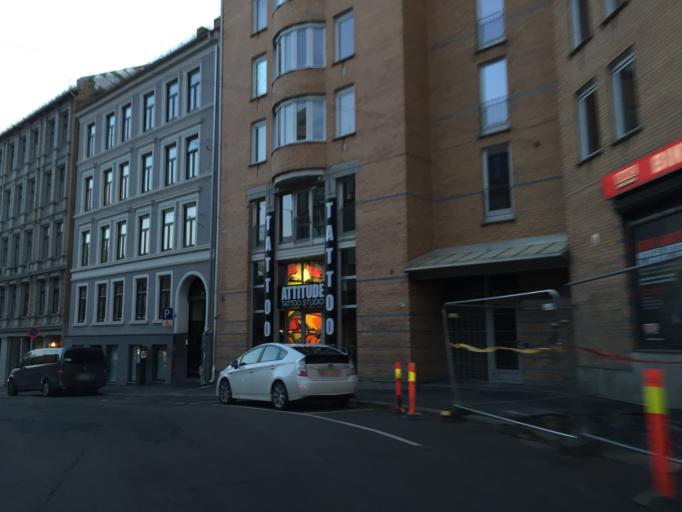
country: NO
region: Oslo
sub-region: Oslo
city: Oslo
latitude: 59.9211
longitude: 10.7326
